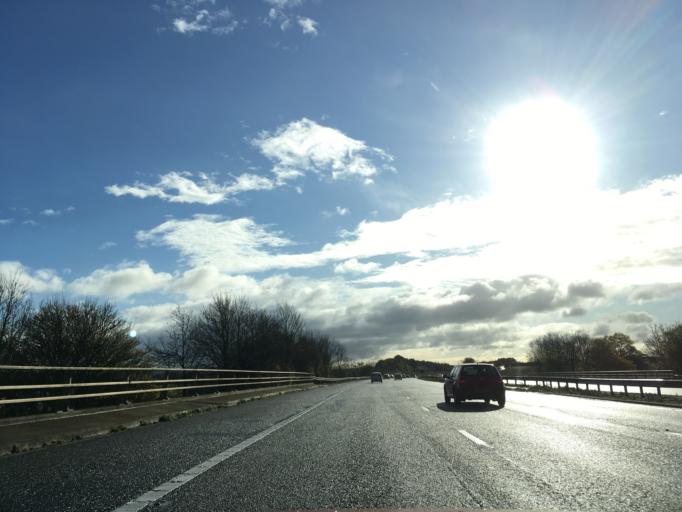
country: GB
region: England
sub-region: Worcestershire
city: Bredon
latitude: 52.0255
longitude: -2.1222
